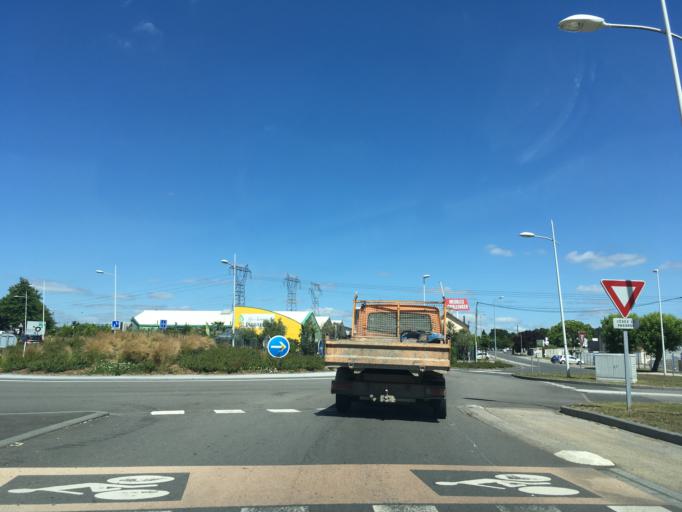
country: FR
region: Pays de la Loire
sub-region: Departement de la Loire-Atlantique
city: Les Sorinieres
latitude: 47.1566
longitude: -1.5385
